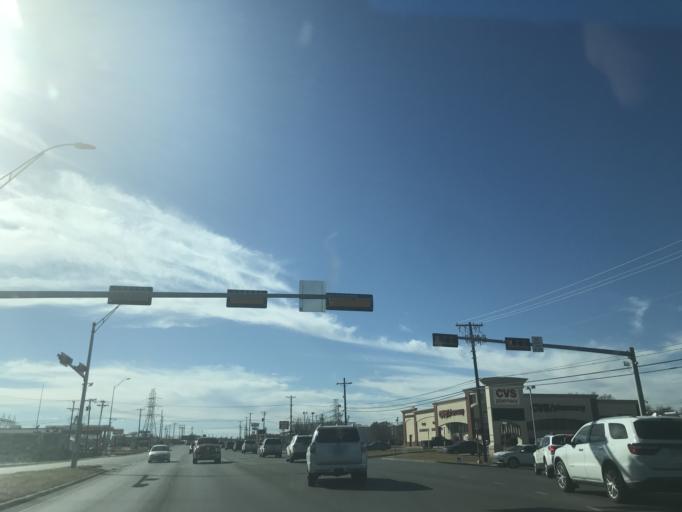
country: US
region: Texas
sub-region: Erath County
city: Stephenville
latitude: 32.2074
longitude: -98.2304
